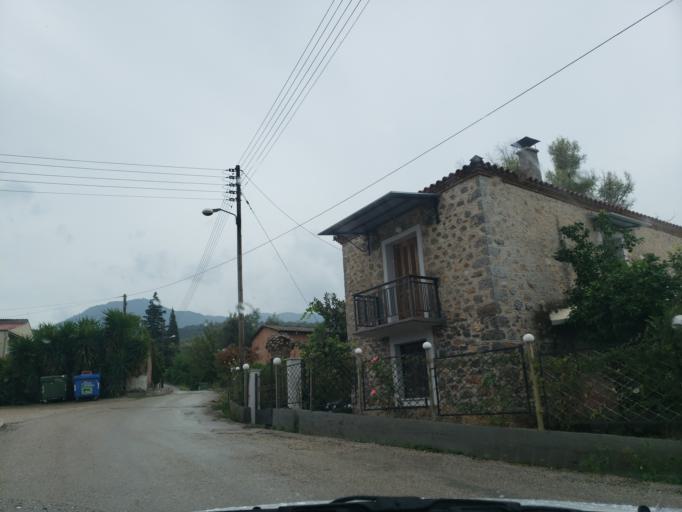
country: GR
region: Central Greece
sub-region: Nomos Fthiotidos
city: Anthili
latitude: 38.7985
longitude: 22.4781
